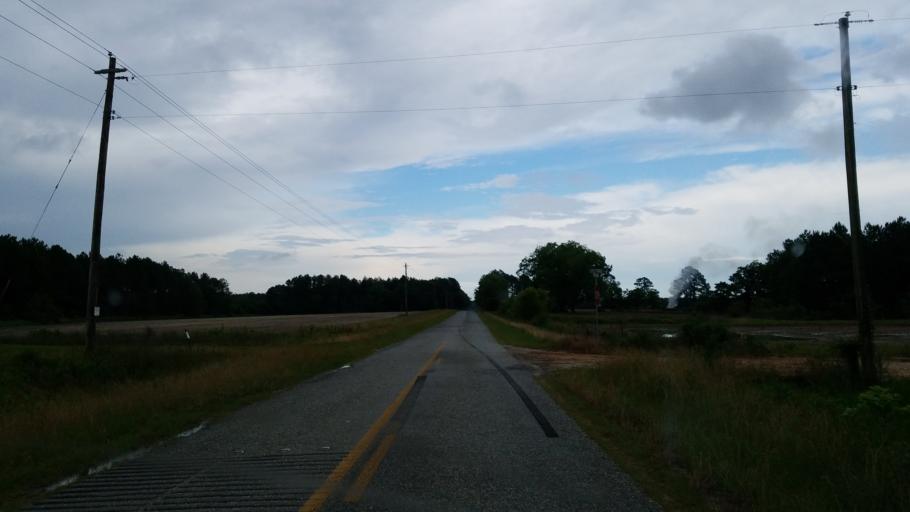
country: US
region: Georgia
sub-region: Crisp County
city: Cordele
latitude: 31.8352
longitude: -83.7836
